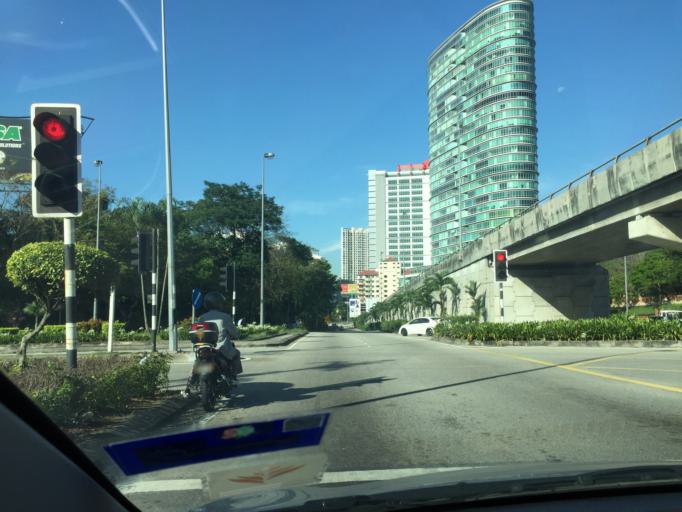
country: MY
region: Selangor
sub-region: Petaling
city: Petaling Jaya
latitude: 3.1320
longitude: 101.6335
